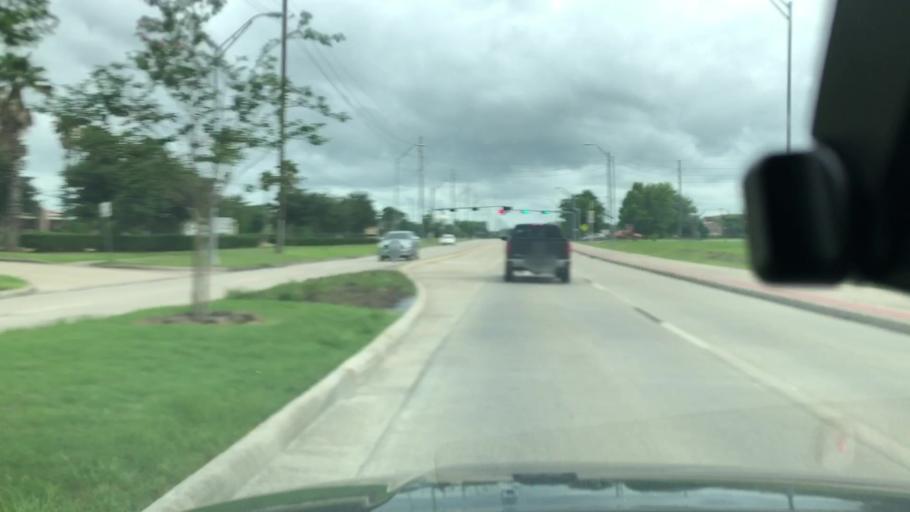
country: US
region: Texas
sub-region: Brazoria County
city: Brookside Village
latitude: 29.5777
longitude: -95.3509
